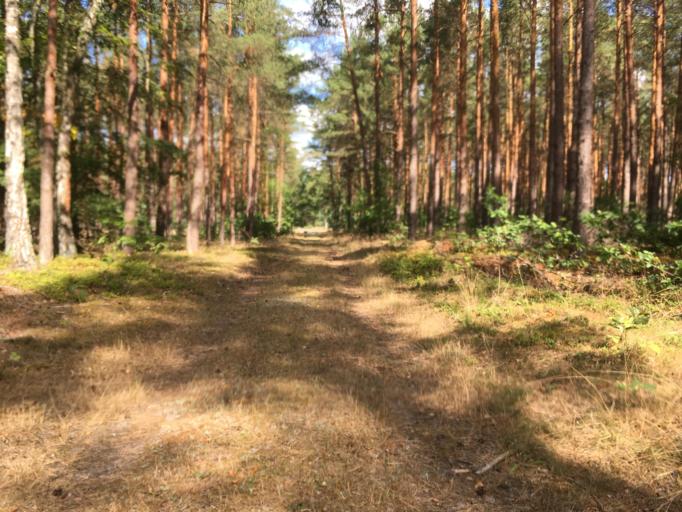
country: DE
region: Brandenburg
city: Zehdenick
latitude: 53.0120
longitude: 13.3670
